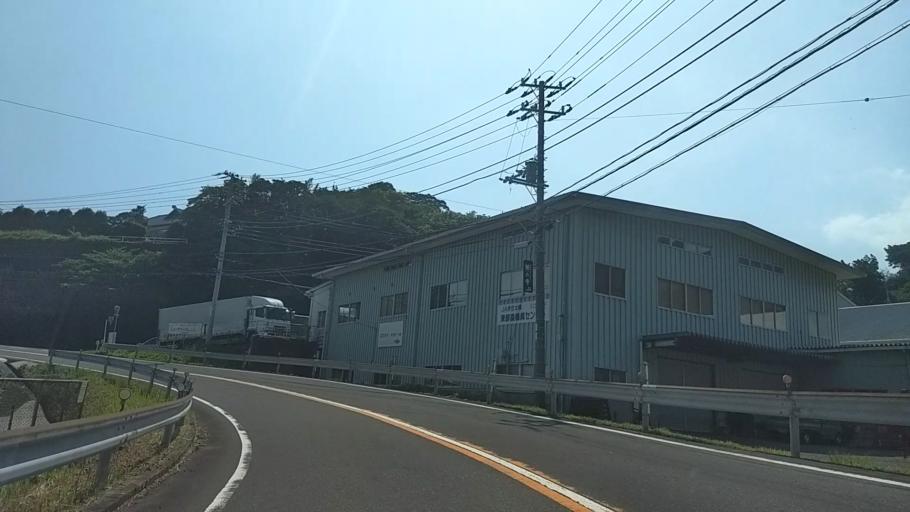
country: JP
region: Shizuoka
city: Shimoda
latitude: 34.7658
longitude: 139.0232
